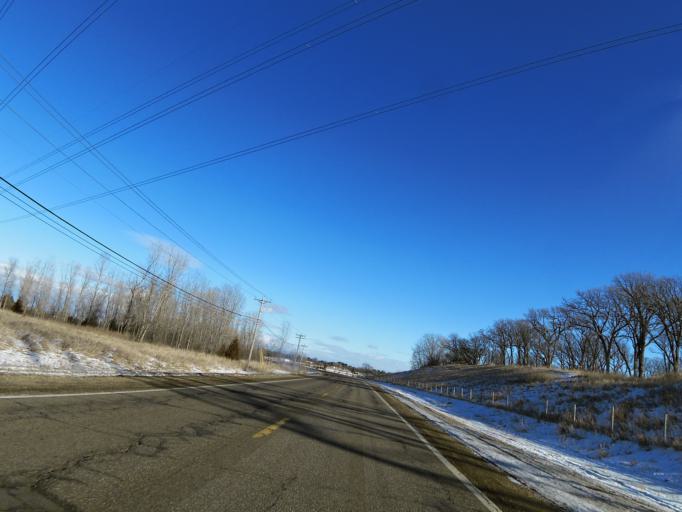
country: US
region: Minnesota
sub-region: Washington County
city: Lakeland
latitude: 44.9469
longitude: -92.8212
